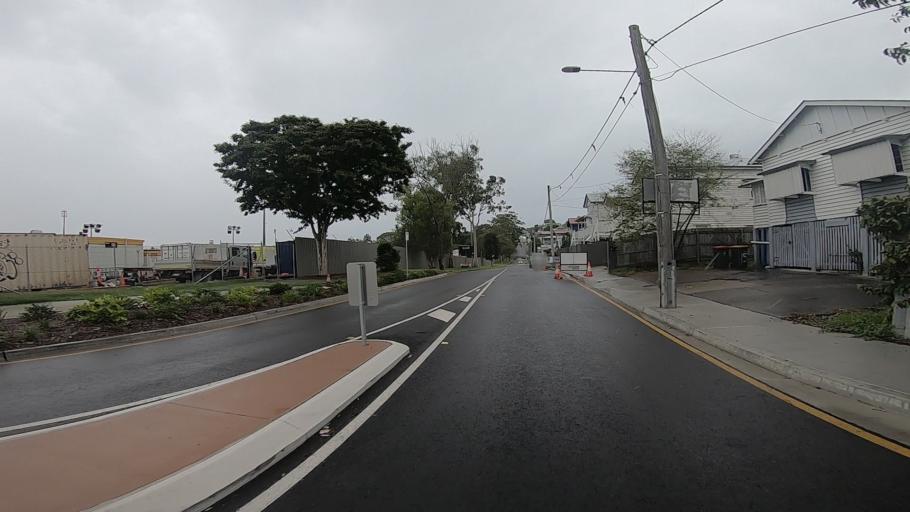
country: AU
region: Queensland
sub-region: Brisbane
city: Ascot
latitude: -27.4392
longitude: 153.0490
